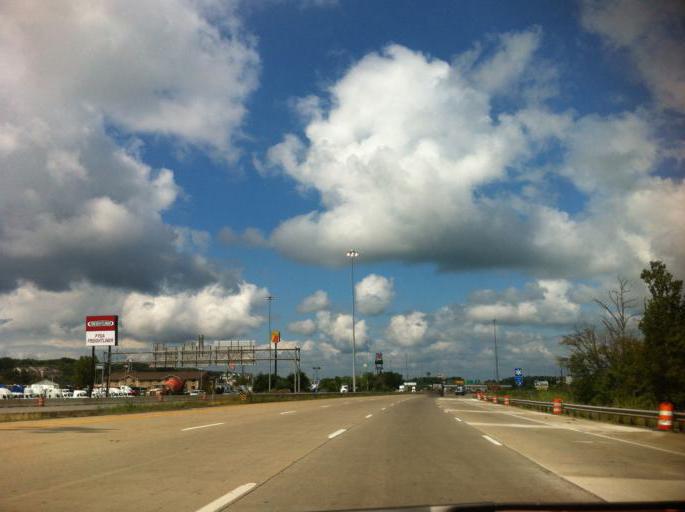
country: US
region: Ohio
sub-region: Trumbull County
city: Mineral Ridge
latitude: 41.1249
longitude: -80.7546
